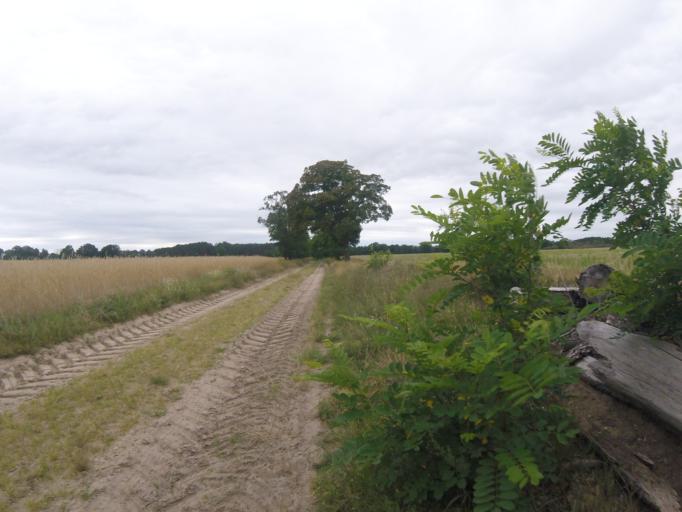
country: DE
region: Brandenburg
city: Mittenwalde
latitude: 52.2531
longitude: 13.5771
